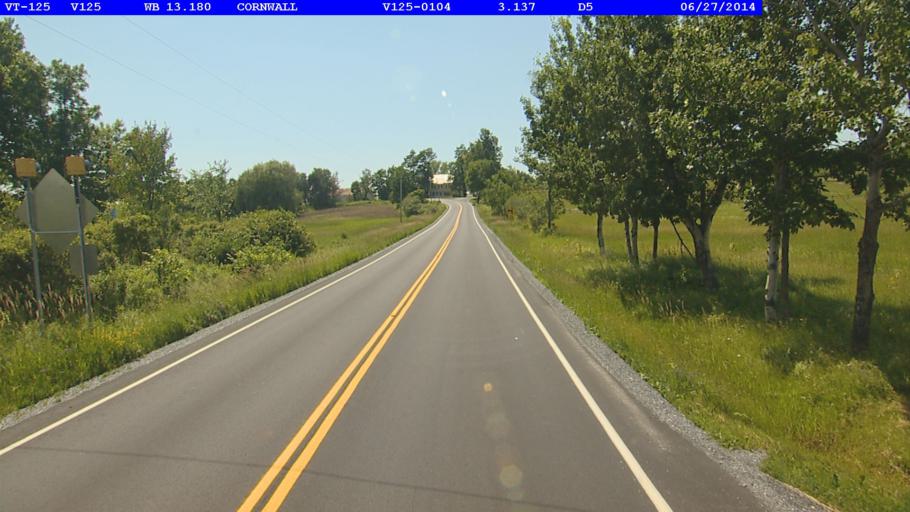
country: US
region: Vermont
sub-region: Addison County
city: Middlebury (village)
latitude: 44.0072
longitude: -73.2111
